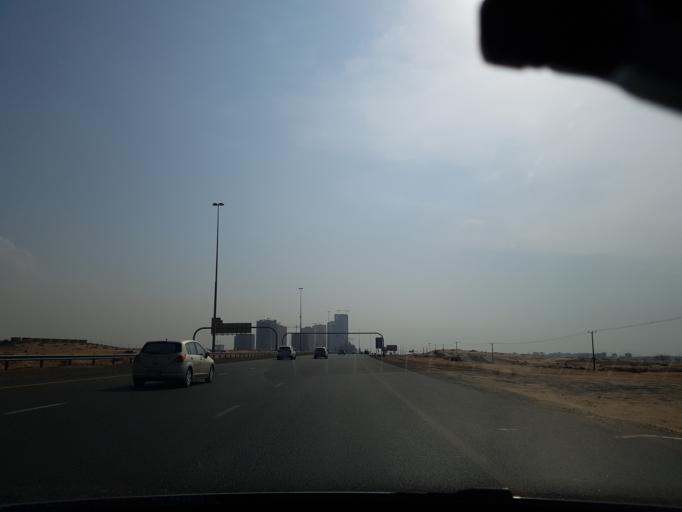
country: AE
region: Ajman
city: Ajman
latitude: 25.4097
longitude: 55.5846
